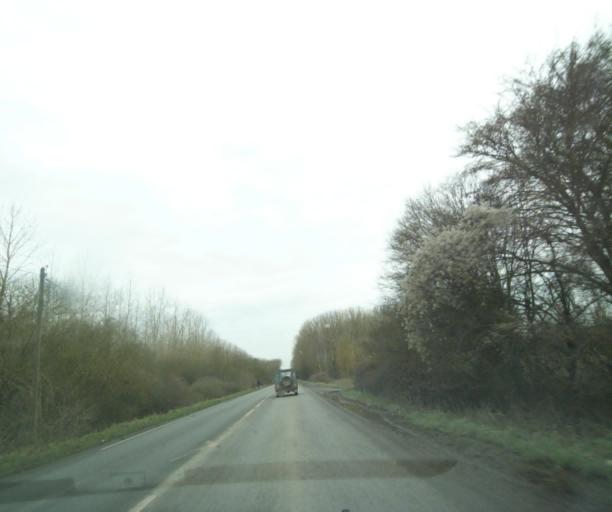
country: FR
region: Nord-Pas-de-Calais
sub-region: Departement du Nord
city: Vicq
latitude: 50.4063
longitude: 3.5917
